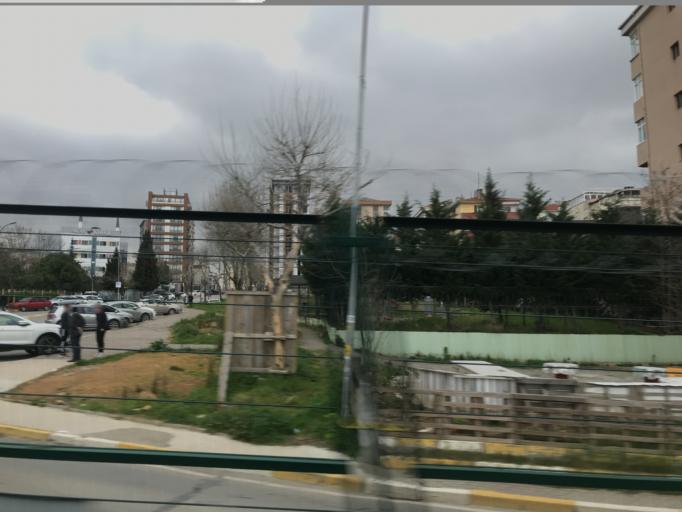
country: TR
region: Istanbul
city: Pendik
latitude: 40.8725
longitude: 29.2542
